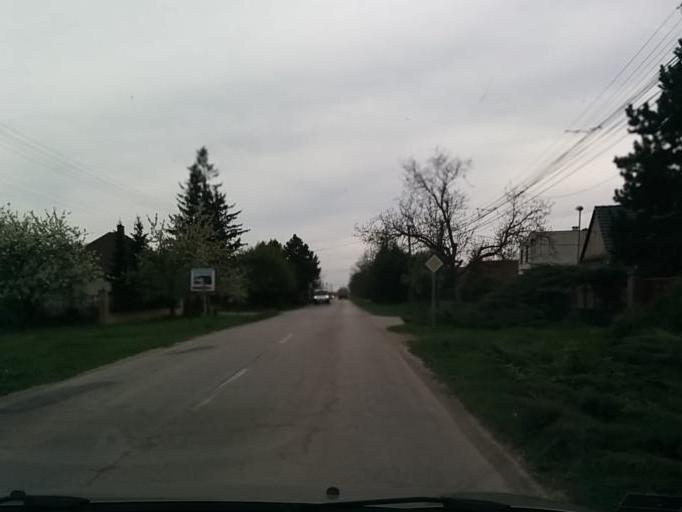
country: SK
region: Bratislavsky
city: Senec
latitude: 48.2458
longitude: 17.4917
